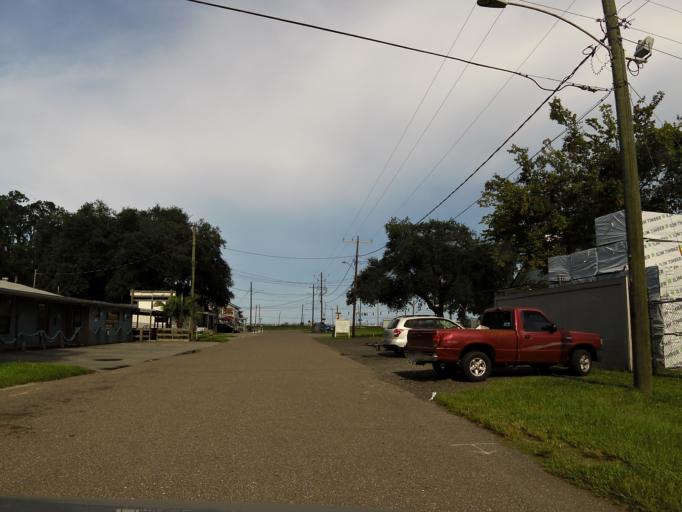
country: US
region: Florida
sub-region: Clay County
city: Orange Park
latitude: 30.2323
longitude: -81.7009
